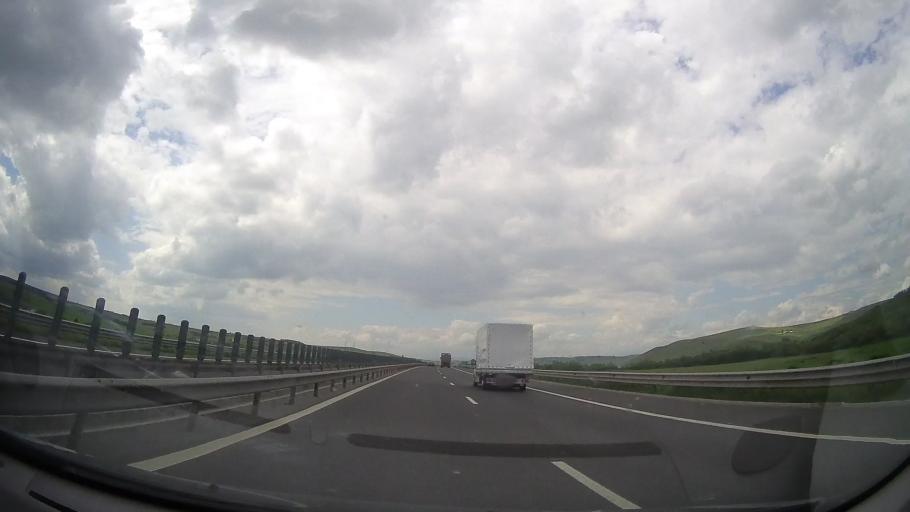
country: RO
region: Alba
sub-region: Comuna Garbova
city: Garbova
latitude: 45.9038
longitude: 23.7524
